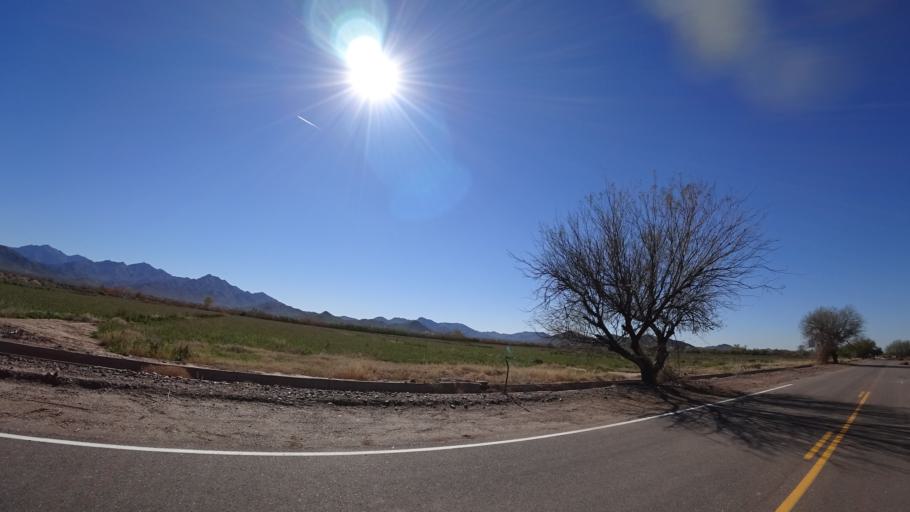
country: US
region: Arizona
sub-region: Maricopa County
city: Avondale
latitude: 33.3919
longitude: -112.3473
